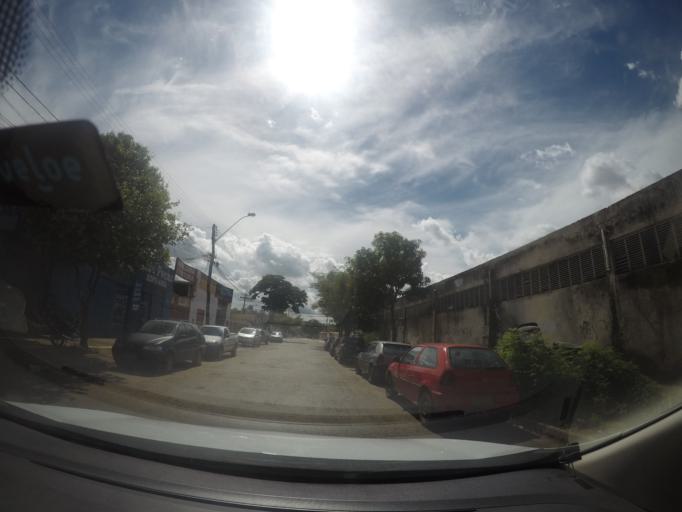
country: BR
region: Goias
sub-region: Goiania
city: Goiania
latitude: -16.6689
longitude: -49.3094
